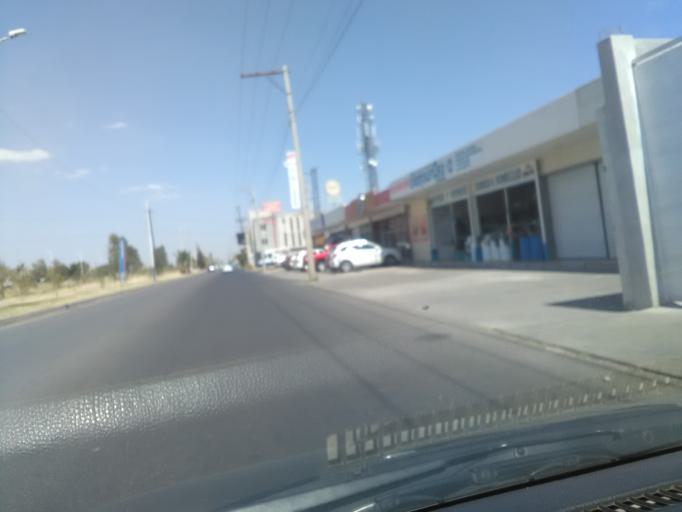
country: MX
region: Durango
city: Victoria de Durango
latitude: 24.0411
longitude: -104.6496
